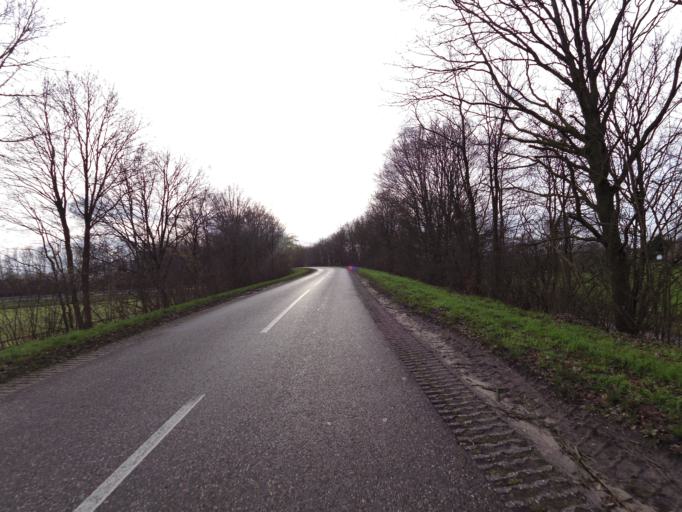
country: NL
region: Gelderland
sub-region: Oude IJsselstreek
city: Wisch
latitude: 51.9460
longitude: 6.4118
